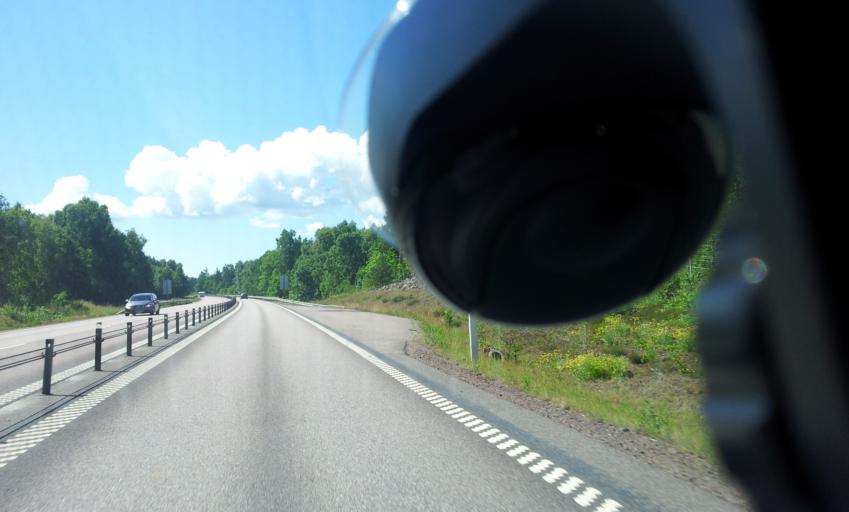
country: SE
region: Kalmar
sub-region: Oskarshamns Kommun
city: Oskarshamn
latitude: 57.2175
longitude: 16.4347
